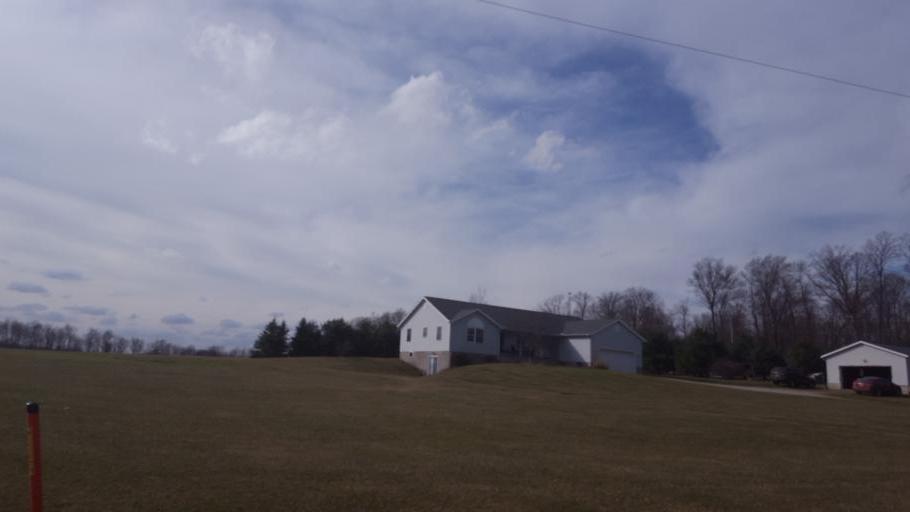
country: US
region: Ohio
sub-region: Sandusky County
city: Bellville
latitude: 40.5490
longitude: -82.4052
